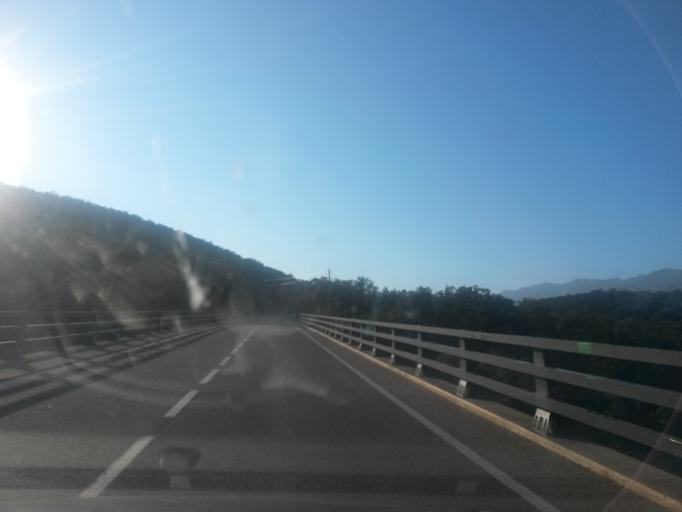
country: ES
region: Catalonia
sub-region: Provincia de Girona
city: Darnius
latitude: 42.3711
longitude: 2.8139
